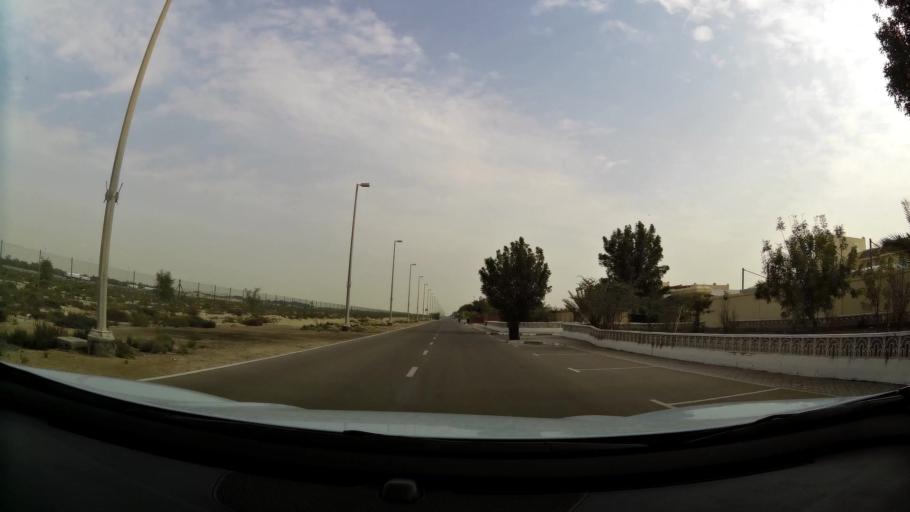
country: AE
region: Abu Dhabi
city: Abu Dhabi
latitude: 24.6744
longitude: 54.7514
